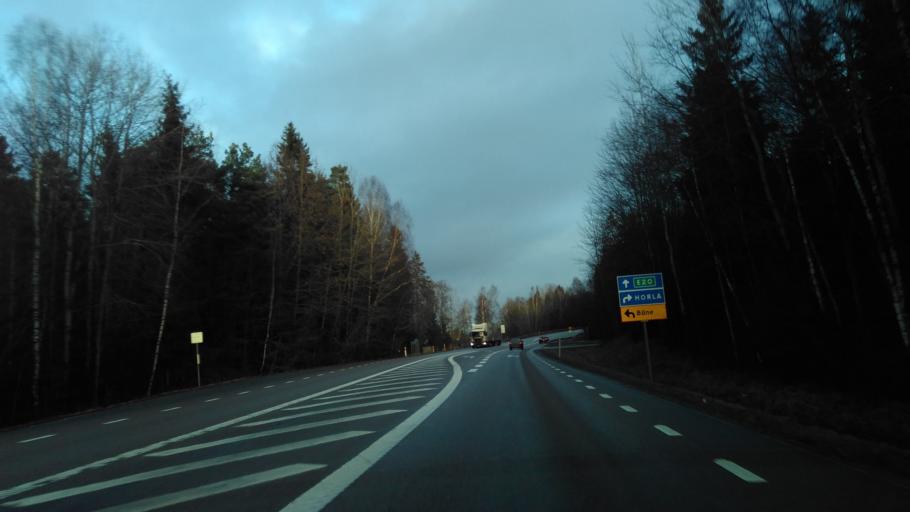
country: SE
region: Vaestra Goetaland
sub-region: Vargarda Kommun
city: Jonstorp
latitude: 57.9889
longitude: 12.6971
